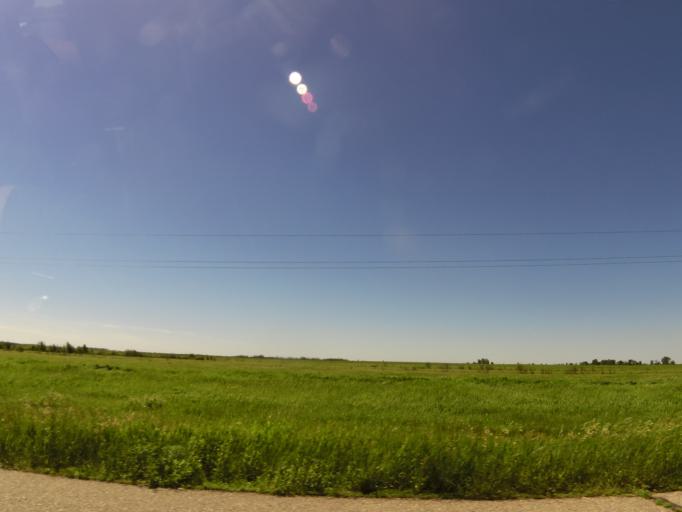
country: US
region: Minnesota
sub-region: Red Lake County
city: Red Lake Falls
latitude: 47.7602
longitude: -96.3281
